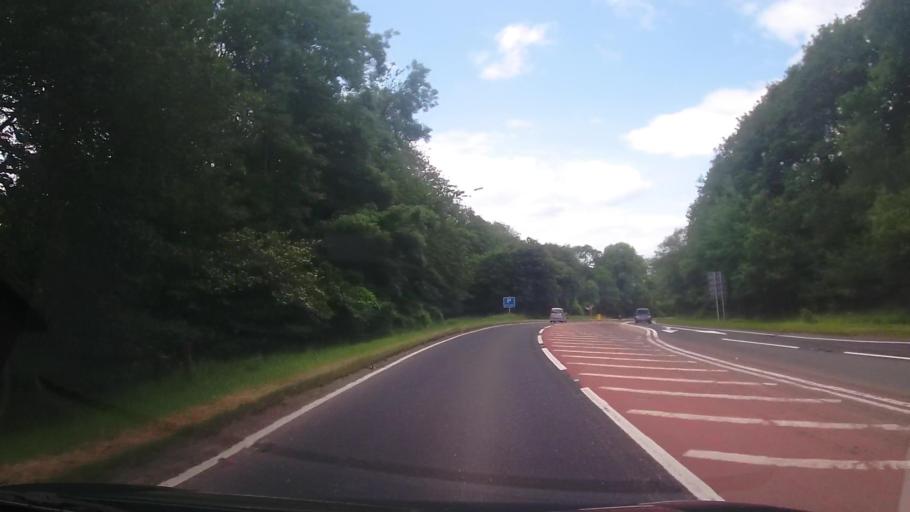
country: GB
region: England
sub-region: Herefordshire
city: Hope under Dinmore
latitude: 52.1605
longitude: -2.7223
